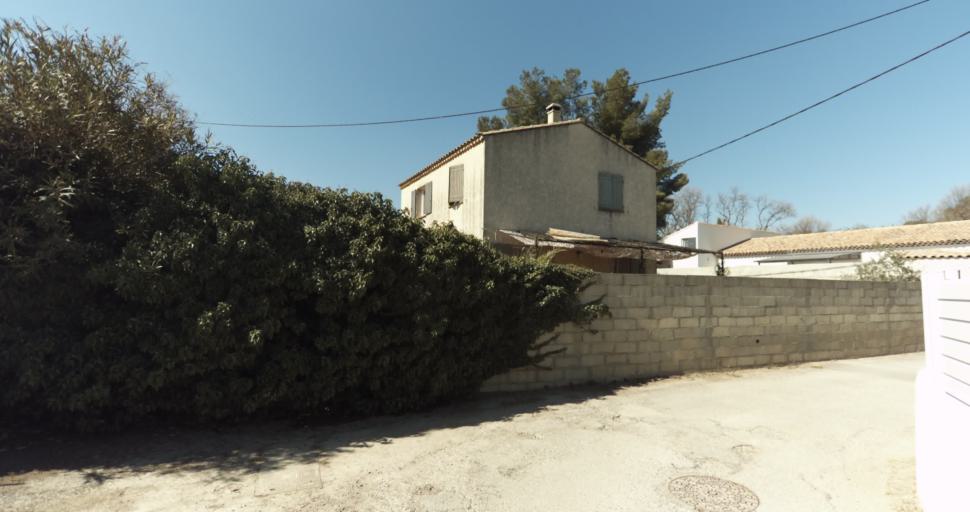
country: FR
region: Provence-Alpes-Cote d'Azur
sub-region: Departement des Bouches-du-Rhone
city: Pelissanne
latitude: 43.6357
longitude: 5.1568
